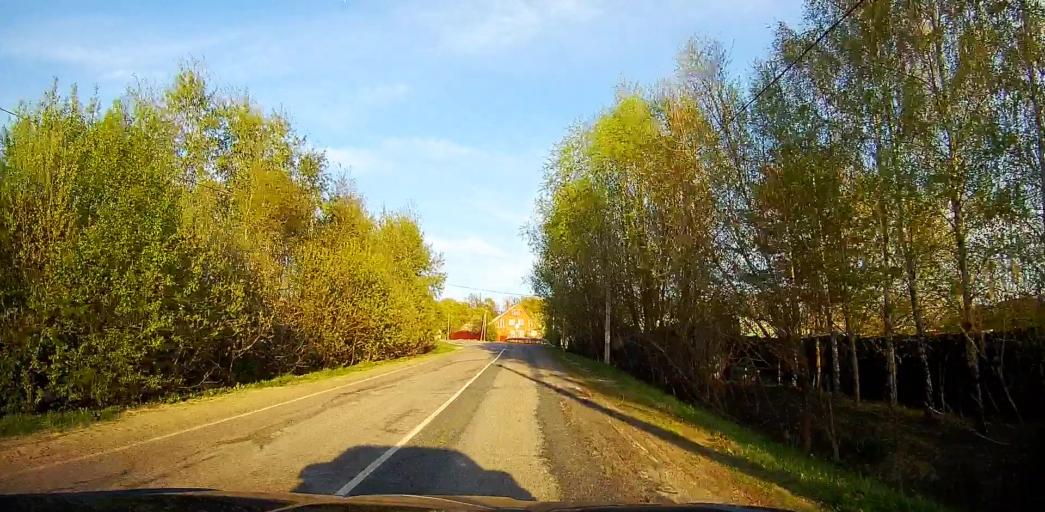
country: RU
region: Moskovskaya
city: Meshcherino
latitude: 55.2438
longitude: 38.3122
